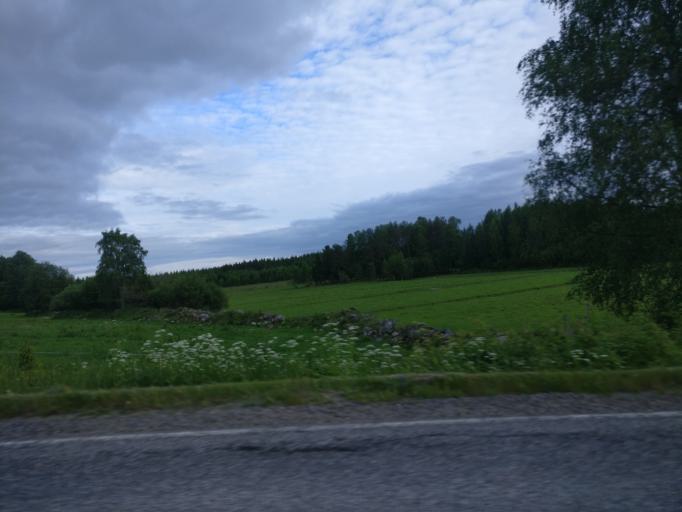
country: FI
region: Southern Savonia
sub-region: Savonlinna
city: Enonkoski
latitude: 61.9721
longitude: 28.9423
